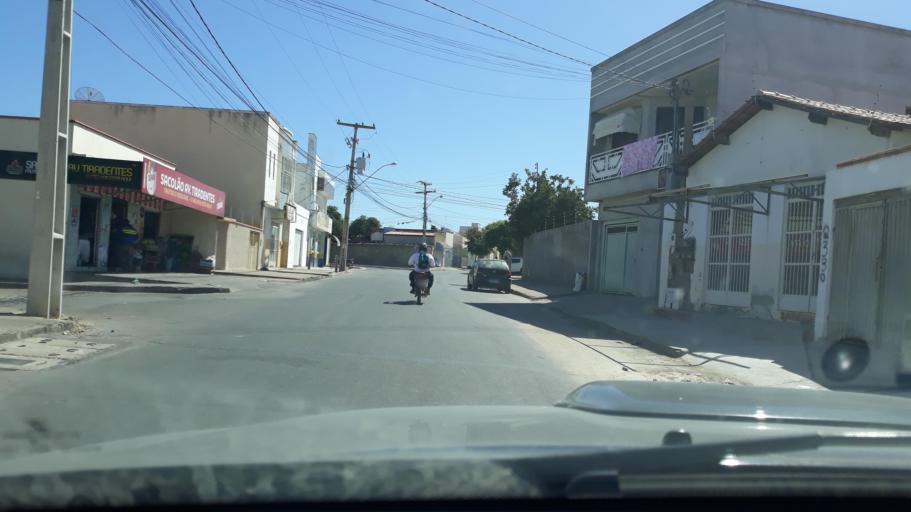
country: BR
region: Bahia
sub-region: Guanambi
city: Guanambi
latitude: -14.2191
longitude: -42.7955
